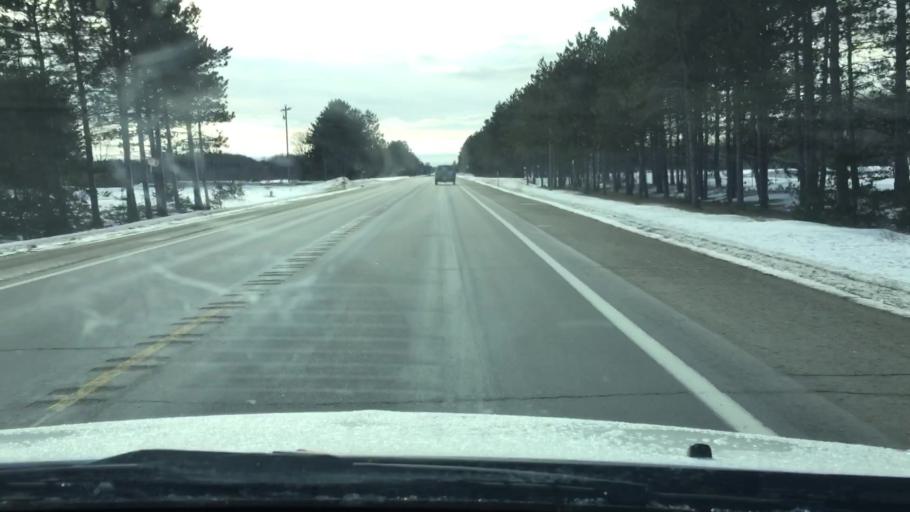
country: US
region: Michigan
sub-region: Kalkaska County
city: Kalkaska
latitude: 44.6858
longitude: -85.2217
